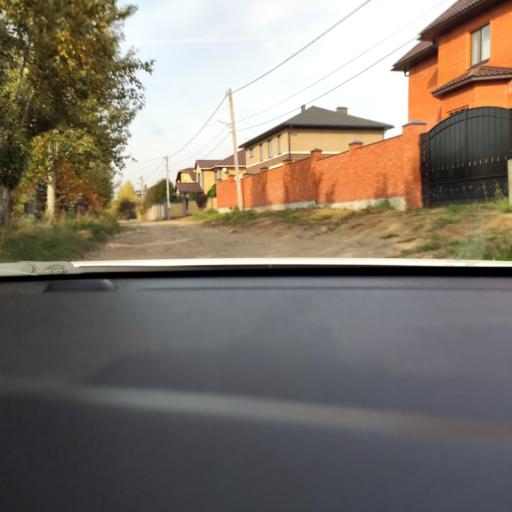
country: RU
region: Tatarstan
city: Vysokaya Gora
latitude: 55.8079
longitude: 49.2457
